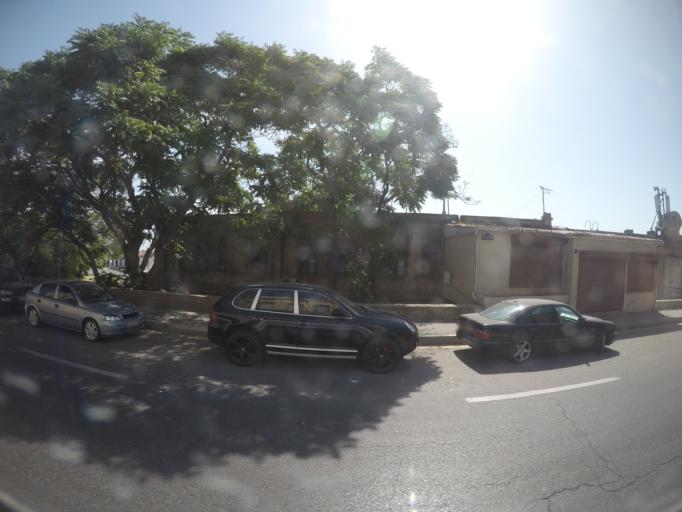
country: AZ
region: Baki
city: Badamdar
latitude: 40.3647
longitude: 49.8261
